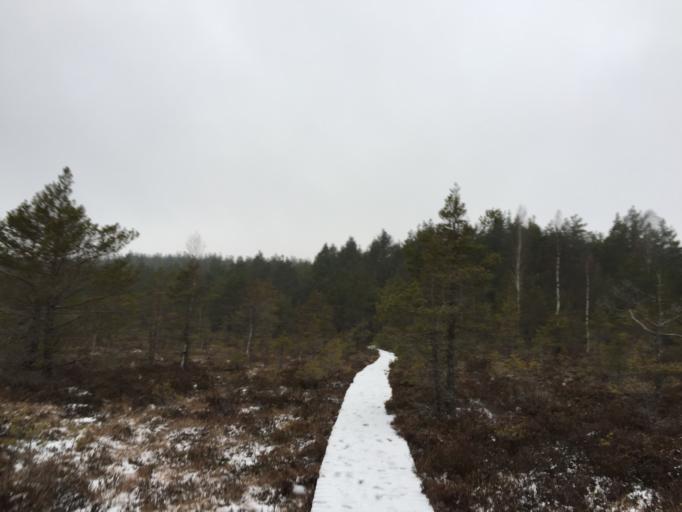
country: EE
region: Paernumaa
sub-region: Paernu linn
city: Parnu
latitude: 58.1374
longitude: 24.5160
